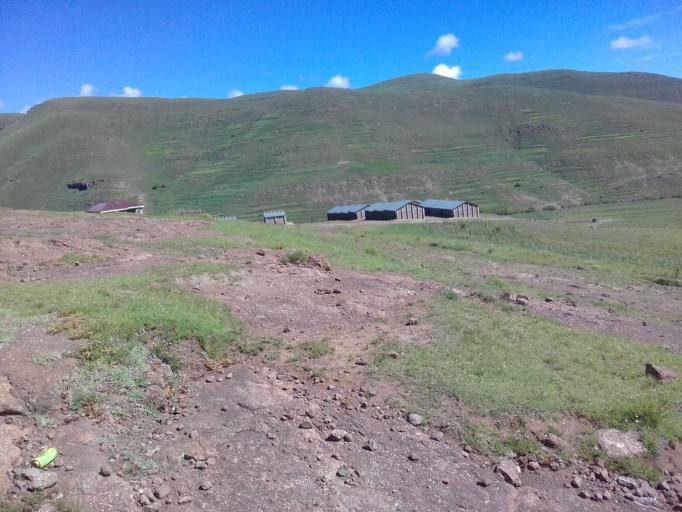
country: LS
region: Thaba-Tseka
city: Thaba-Tseka
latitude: -29.5241
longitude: 28.5840
